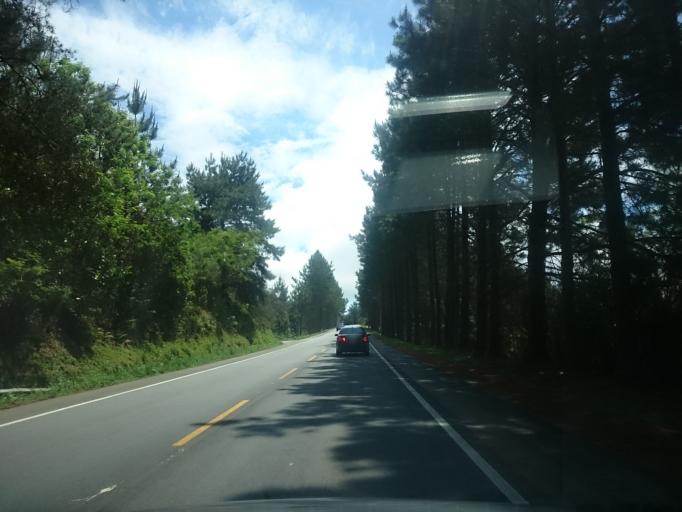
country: BR
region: Santa Catarina
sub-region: Santo Amaro Da Imperatriz
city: Santo Amaro da Imperatriz
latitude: -27.6780
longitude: -49.0113
